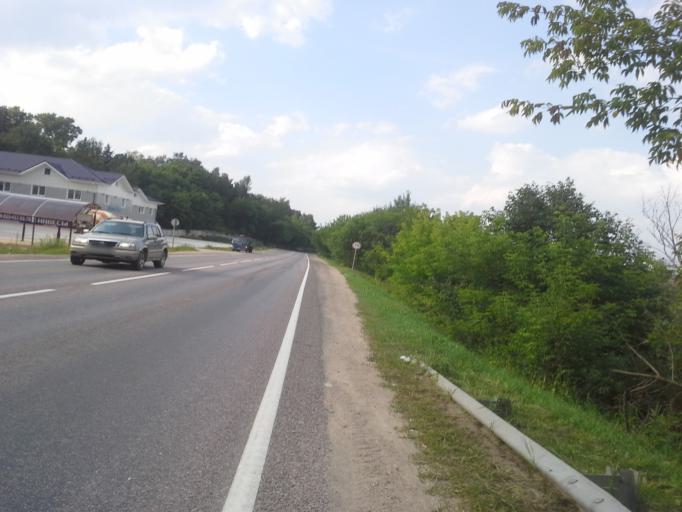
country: RU
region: Moskovskaya
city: Istra
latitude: 55.9010
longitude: 36.8084
